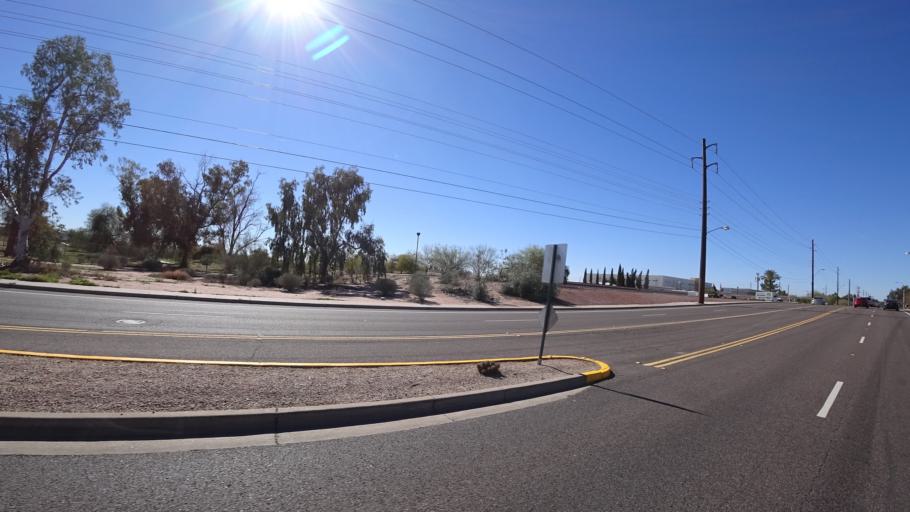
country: US
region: Arizona
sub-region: Maricopa County
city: Tempe
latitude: 33.4512
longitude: -111.9136
